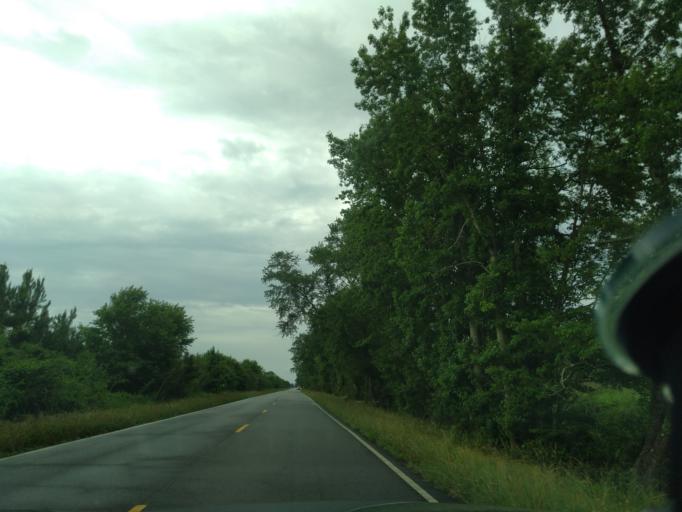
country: US
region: North Carolina
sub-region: Washington County
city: Plymouth
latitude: 35.8526
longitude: -76.5663
